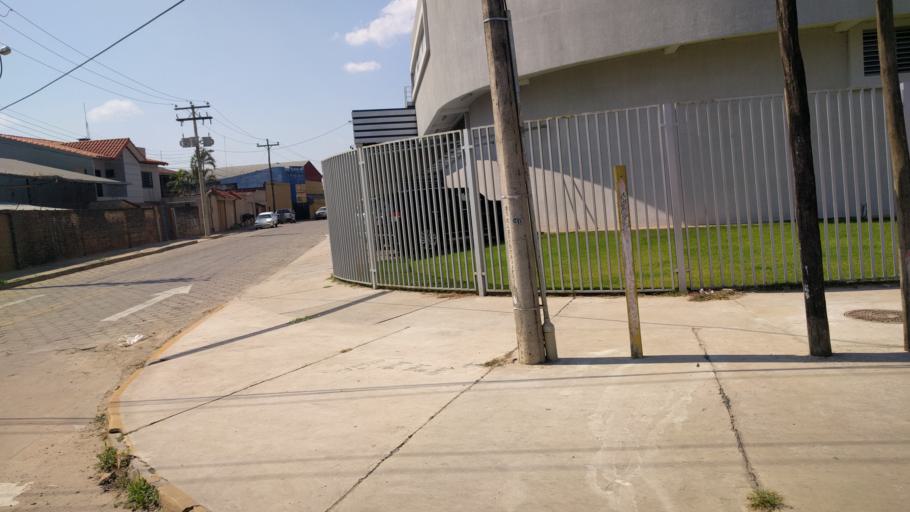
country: BO
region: Santa Cruz
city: Santa Cruz de la Sierra
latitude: -17.7273
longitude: -63.1663
